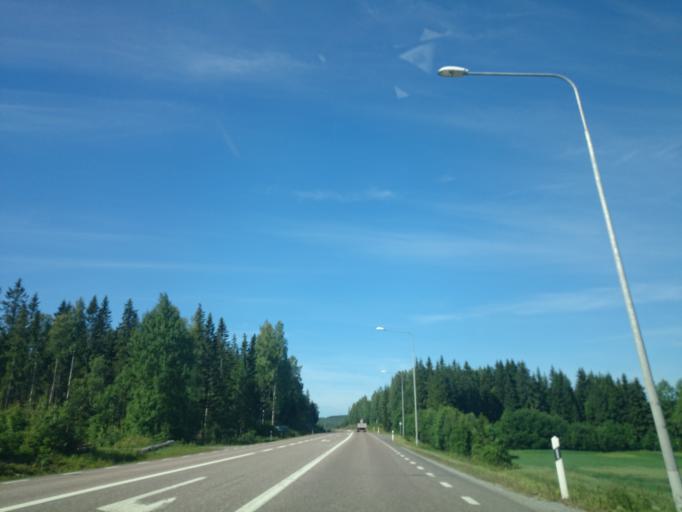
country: SE
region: Vaesternorrland
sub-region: Sundsvalls Kommun
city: Vi
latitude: 62.3769
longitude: 17.1336
